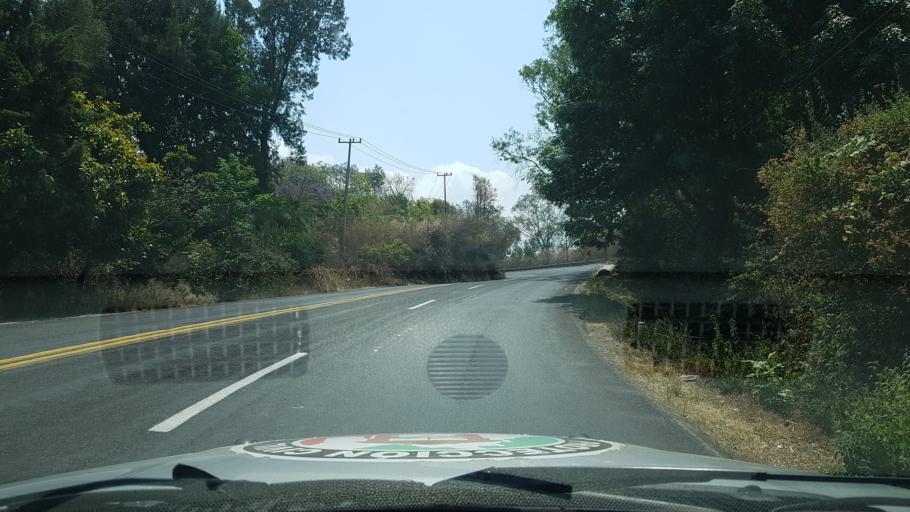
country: MX
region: Mexico
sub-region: Tepetlixpa
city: Nepantla de Sor Juana Ines de la Cruz
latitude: 18.9893
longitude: -98.8303
